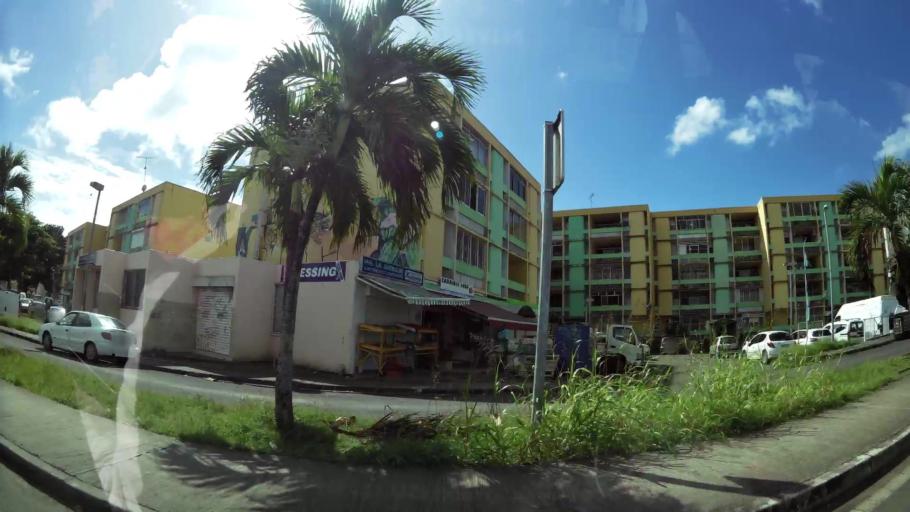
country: GP
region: Guadeloupe
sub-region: Guadeloupe
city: Pointe-a-Pitre
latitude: 16.2491
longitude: -61.5349
